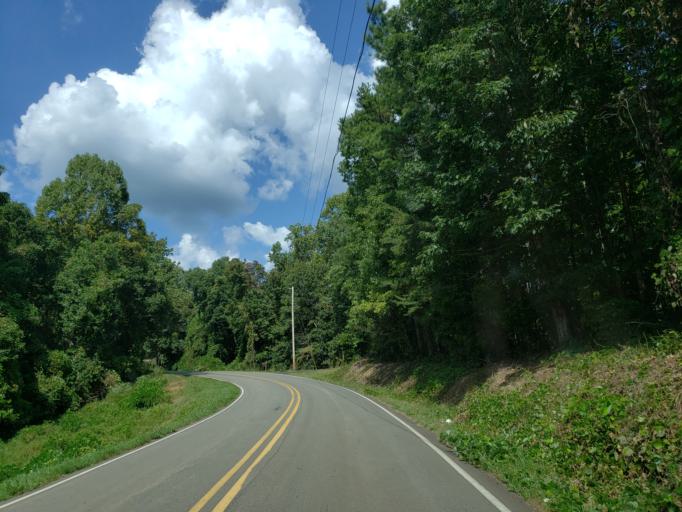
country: US
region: Georgia
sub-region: Pickens County
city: Jasper
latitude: 34.4199
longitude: -84.4456
